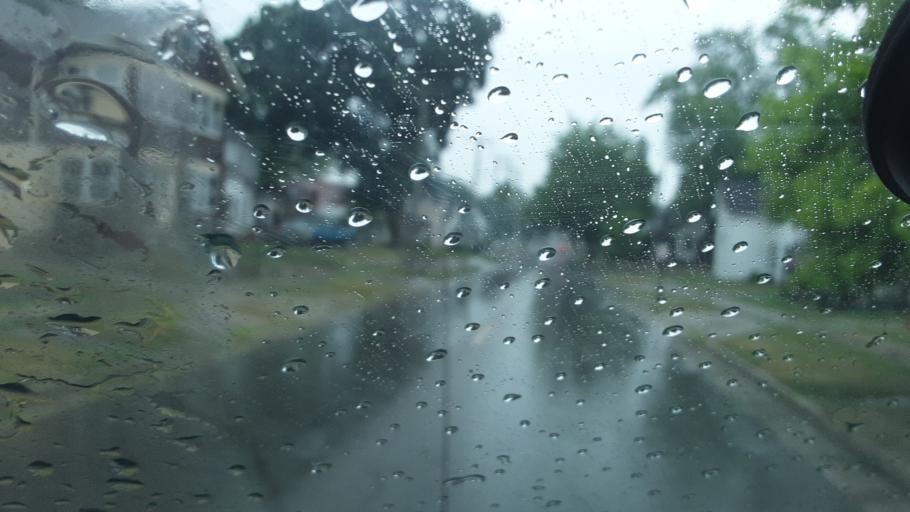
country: US
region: Ohio
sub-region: Williams County
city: Montpelier
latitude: 41.5848
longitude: -84.6071
